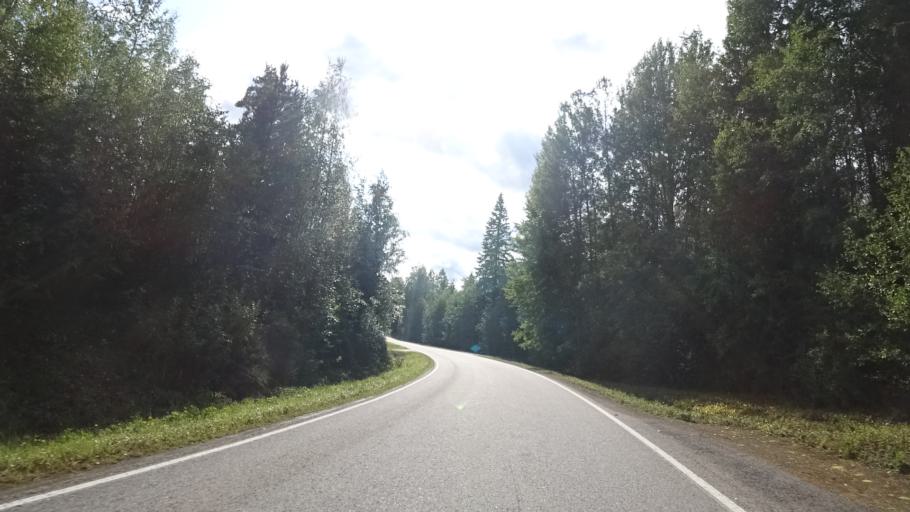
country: RU
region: Republic of Karelia
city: Vyartsilya
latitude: 62.2279
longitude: 30.6641
